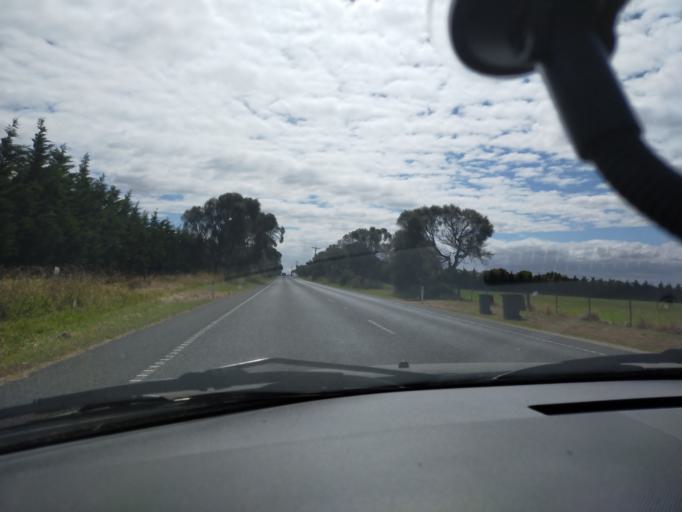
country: AU
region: Victoria
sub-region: Greater Geelong
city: Leopold
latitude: -38.2588
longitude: 144.4188
